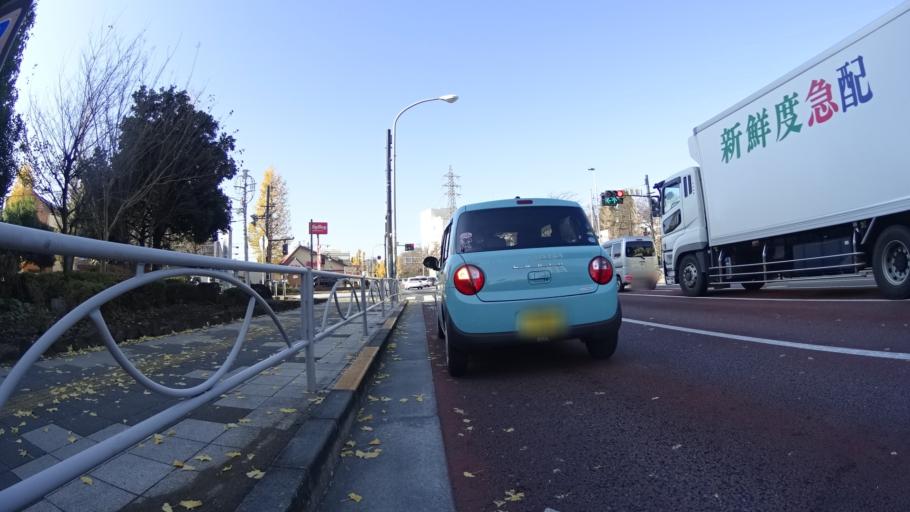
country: JP
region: Tokyo
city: Hino
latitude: 35.6674
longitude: 139.3778
